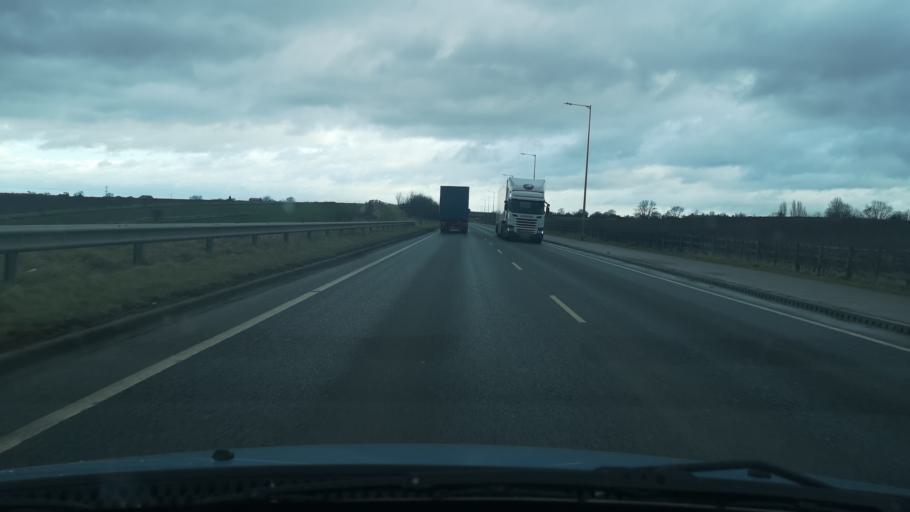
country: GB
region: England
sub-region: Barnsley
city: Cudworth
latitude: 53.5810
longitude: -1.4196
